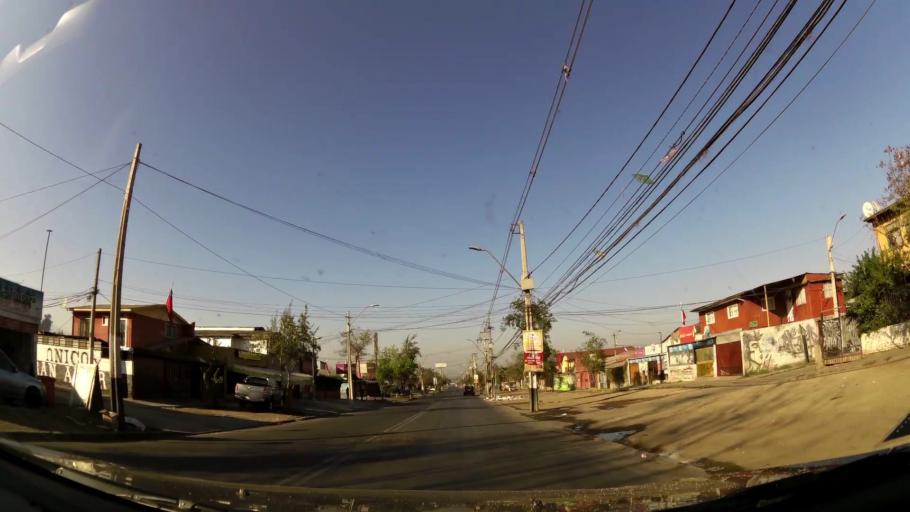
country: CL
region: Santiago Metropolitan
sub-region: Provincia de Chacabuco
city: Chicureo Abajo
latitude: -33.3657
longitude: -70.6334
